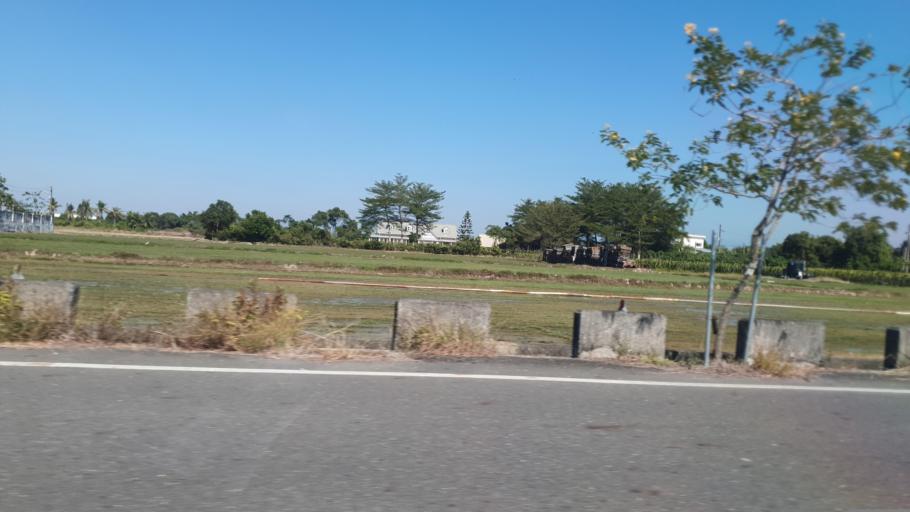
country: TW
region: Taiwan
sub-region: Tainan
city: Tainan
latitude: 23.0385
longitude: 120.3311
